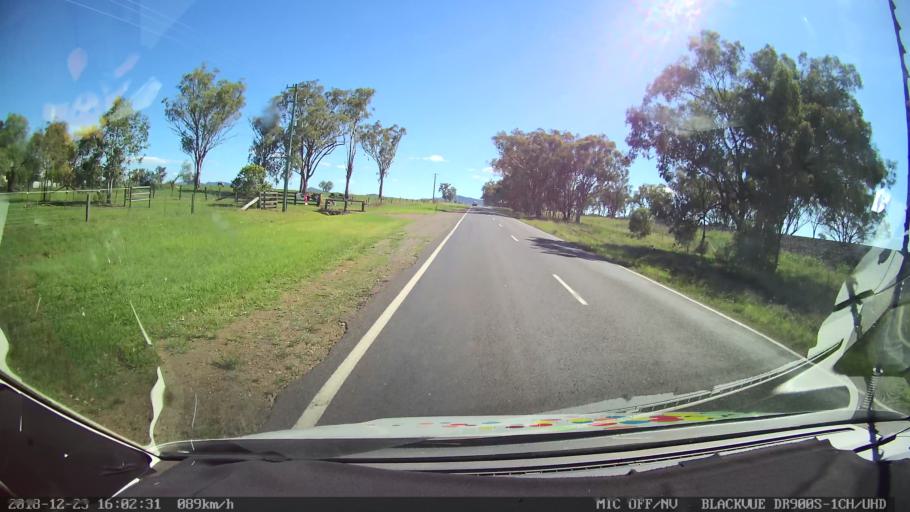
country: AU
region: New South Wales
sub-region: Tamworth Municipality
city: Phillip
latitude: -31.2331
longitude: 150.8084
